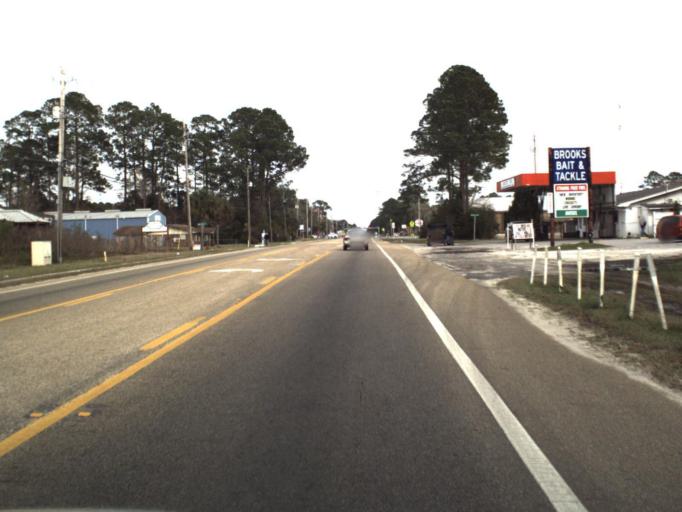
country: US
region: Florida
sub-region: Bay County
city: Callaway
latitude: 30.1529
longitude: -85.5732
